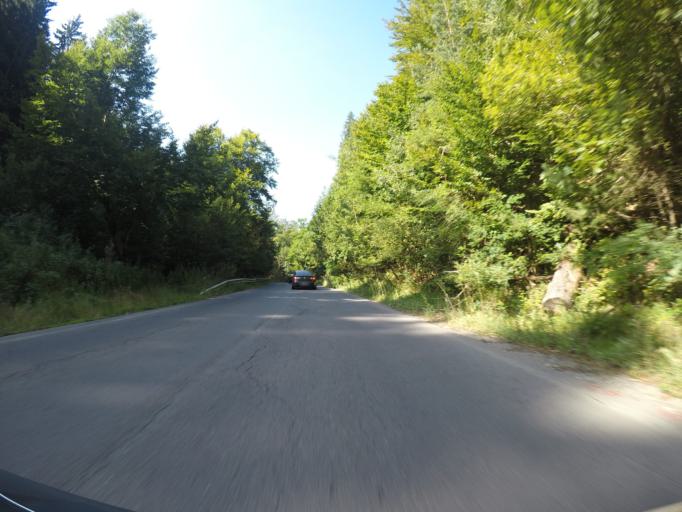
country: RO
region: Brasov
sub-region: Comuna Cristian
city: Cristian
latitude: 45.5948
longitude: 25.5370
